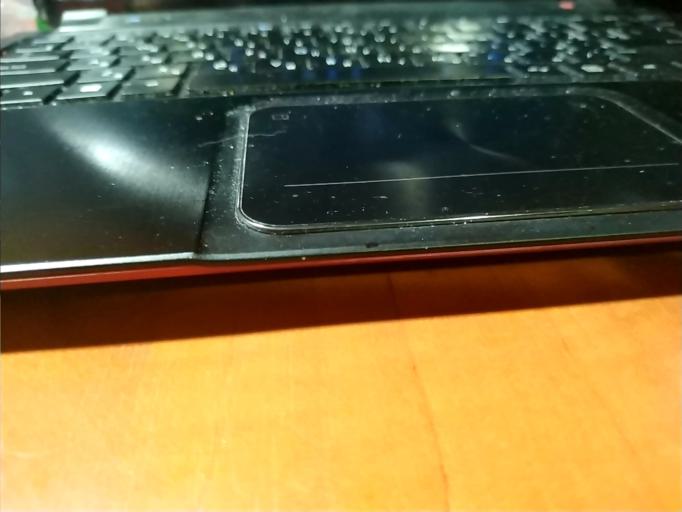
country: RU
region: Tverskaya
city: Ves'yegonsk
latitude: 58.7079
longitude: 37.5439
